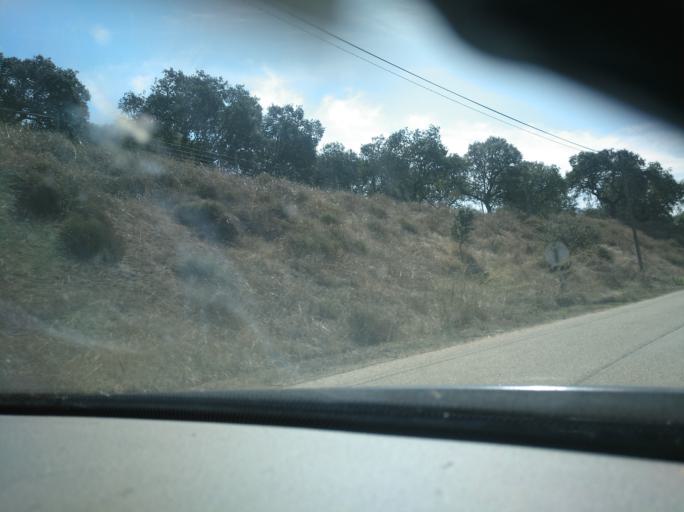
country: PT
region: Evora
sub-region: Montemor-O-Novo
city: Montemor-o-Novo
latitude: 38.6653
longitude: -8.0944
